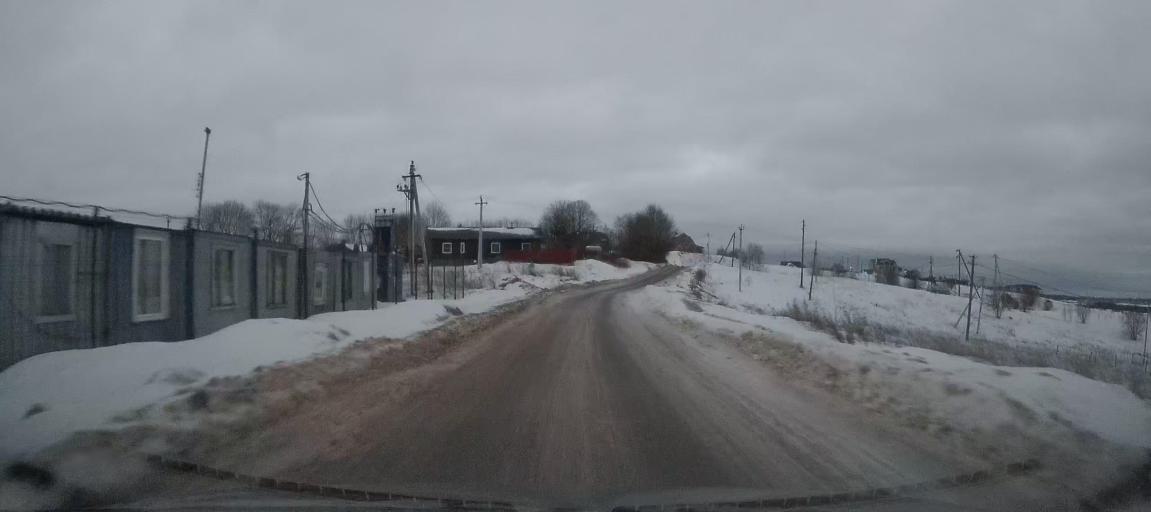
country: RU
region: Leningrad
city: Taytsy
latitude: 59.6959
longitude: 30.1440
